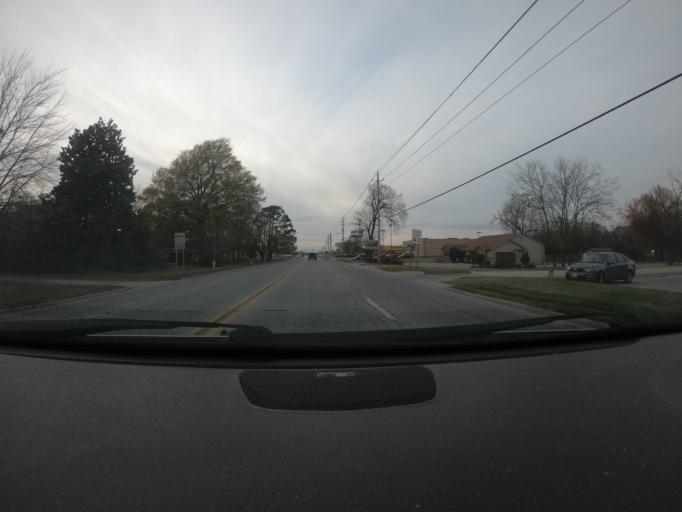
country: US
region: Arkansas
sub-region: Benton County
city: Rogers
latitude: 36.3339
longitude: -94.1402
